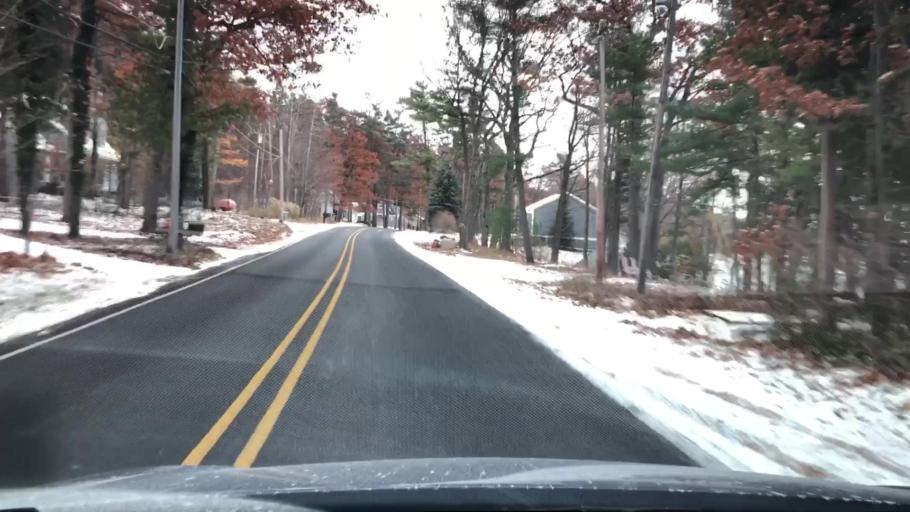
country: US
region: Michigan
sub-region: Grand Traverse County
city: Traverse City
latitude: 44.8162
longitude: -85.5786
